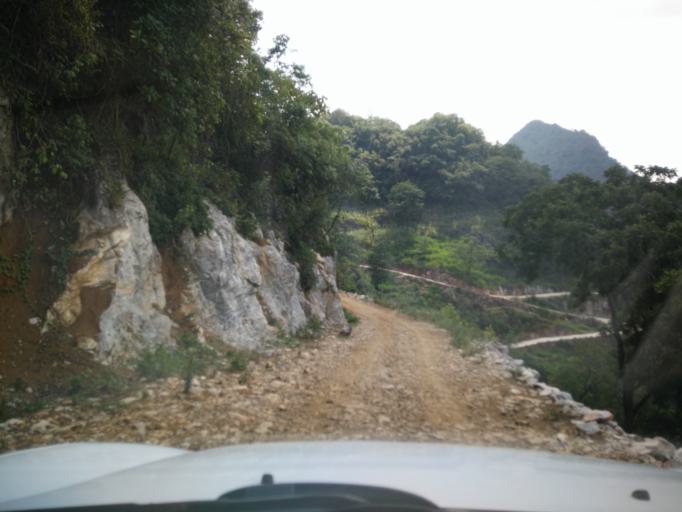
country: CN
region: Guangxi Zhuangzu Zizhiqu
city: Xinzhou
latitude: 25.1353
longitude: 105.6768
